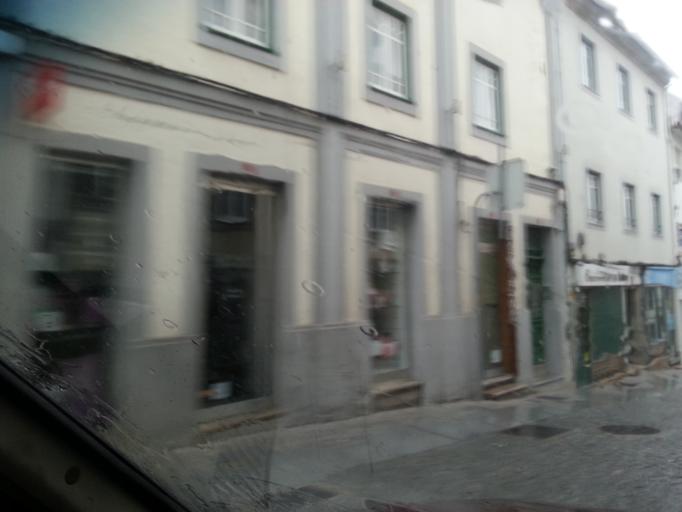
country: PT
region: Guarda
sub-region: Guarda
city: Guarda
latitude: 40.5389
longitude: -7.2676
